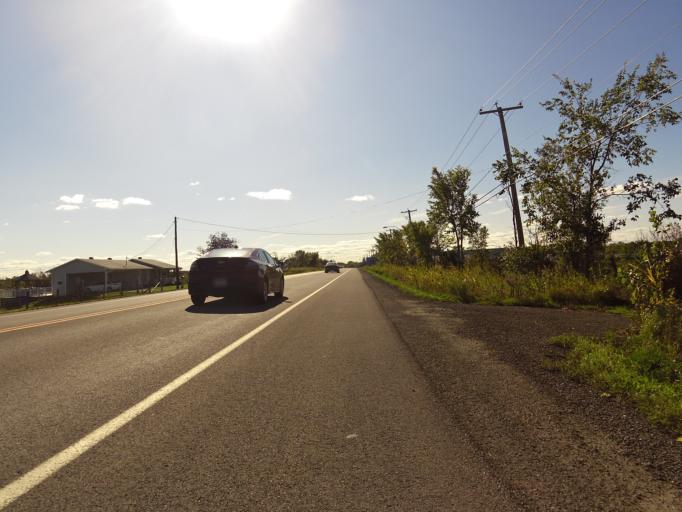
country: CA
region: Quebec
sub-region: Outaouais
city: Gatineau
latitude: 45.5139
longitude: -75.5300
